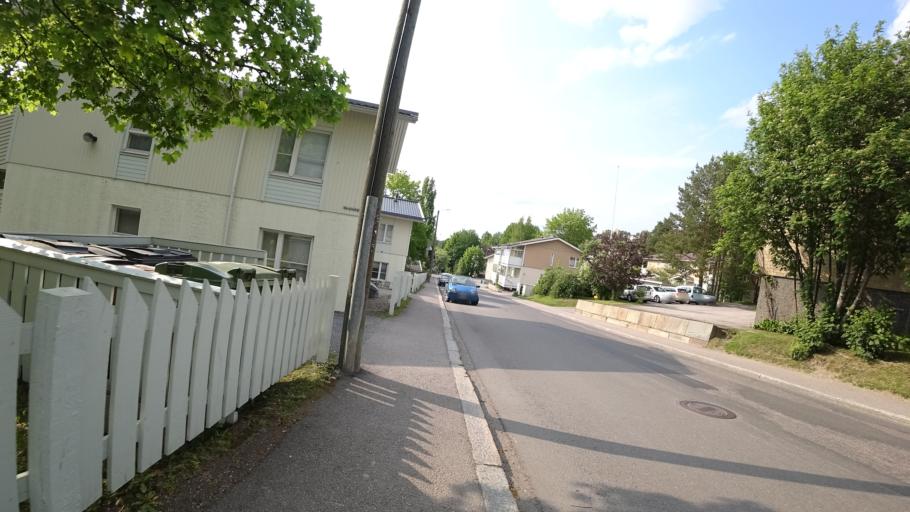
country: FI
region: Pirkanmaa
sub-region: Tampere
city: Tampere
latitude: 61.4985
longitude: 23.7152
